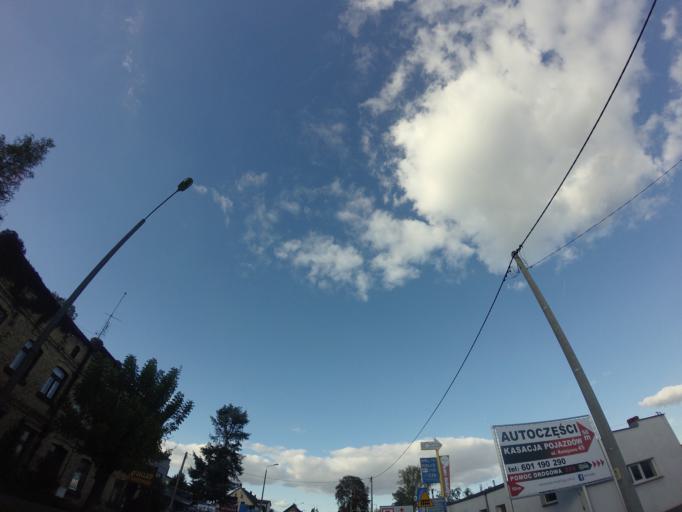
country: PL
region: Greater Poland Voivodeship
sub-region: Powiat nowotomyski
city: Nowy Tomysl
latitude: 52.3030
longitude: 16.1280
